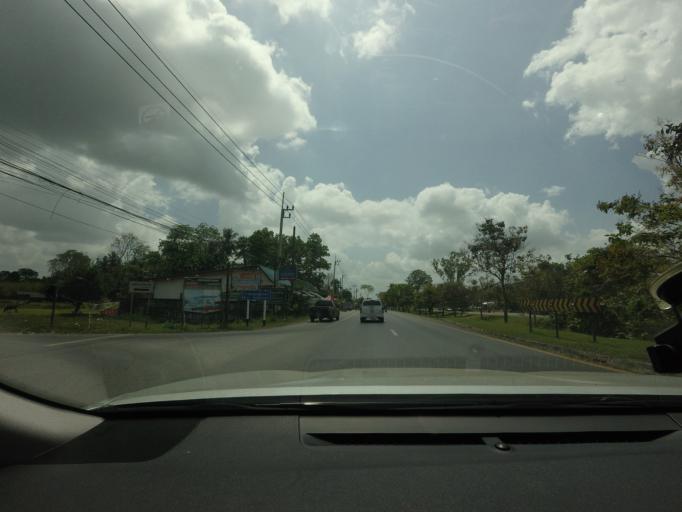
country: TH
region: Nakhon Si Thammarat
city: Nakhon Si Thammarat
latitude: 8.4255
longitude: 99.9216
